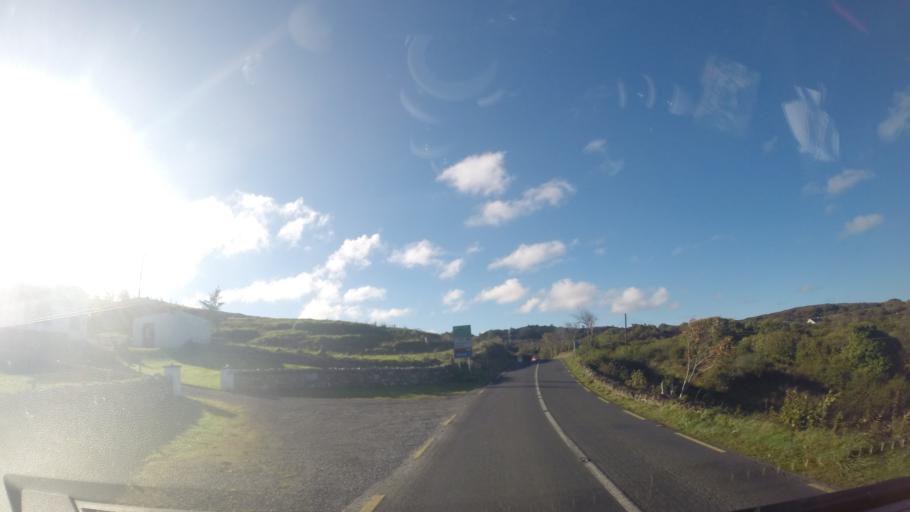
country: IE
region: Ulster
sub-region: County Donegal
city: Dungloe
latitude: 54.8318
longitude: -8.3673
